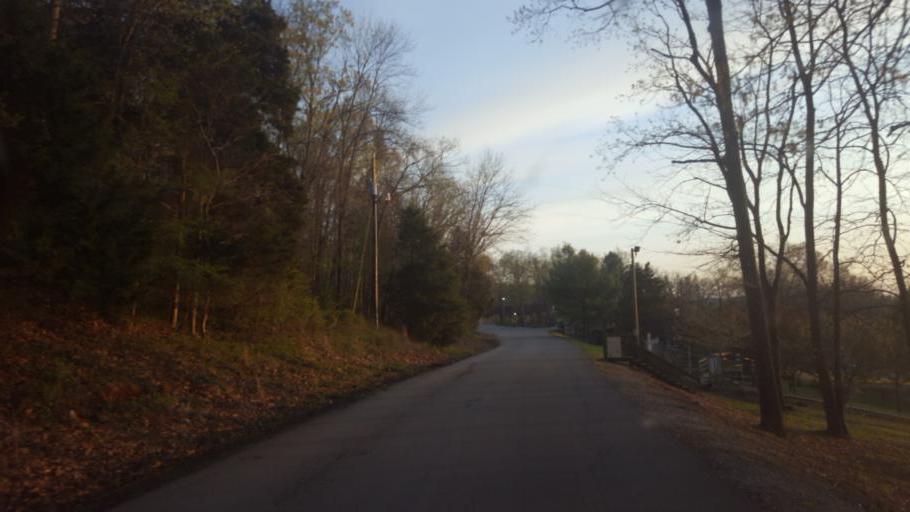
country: US
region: Kentucky
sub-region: Barren County
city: Cave City
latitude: 37.1365
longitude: -85.9962
